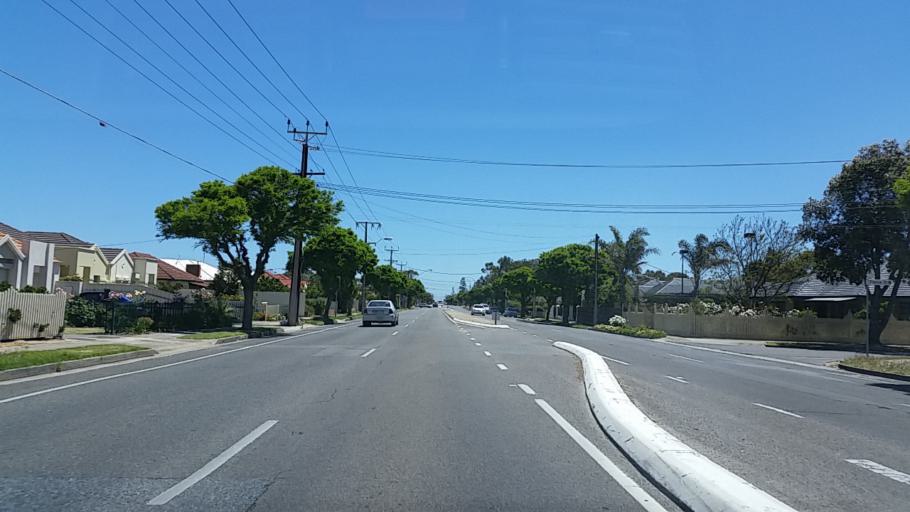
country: AU
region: South Australia
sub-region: Charles Sturt
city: Grange
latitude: -34.9070
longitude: 138.5017
